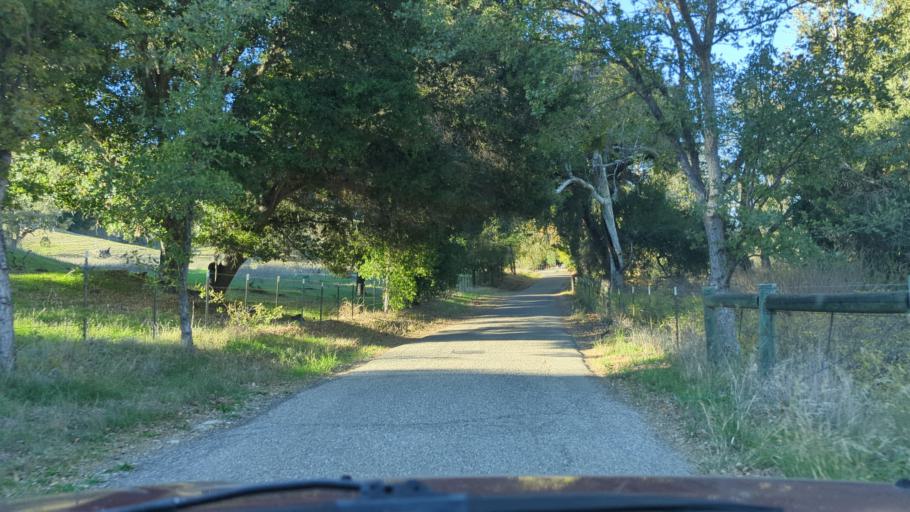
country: US
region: California
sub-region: Santa Barbara County
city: Santa Ynez
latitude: 34.5658
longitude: -120.0942
